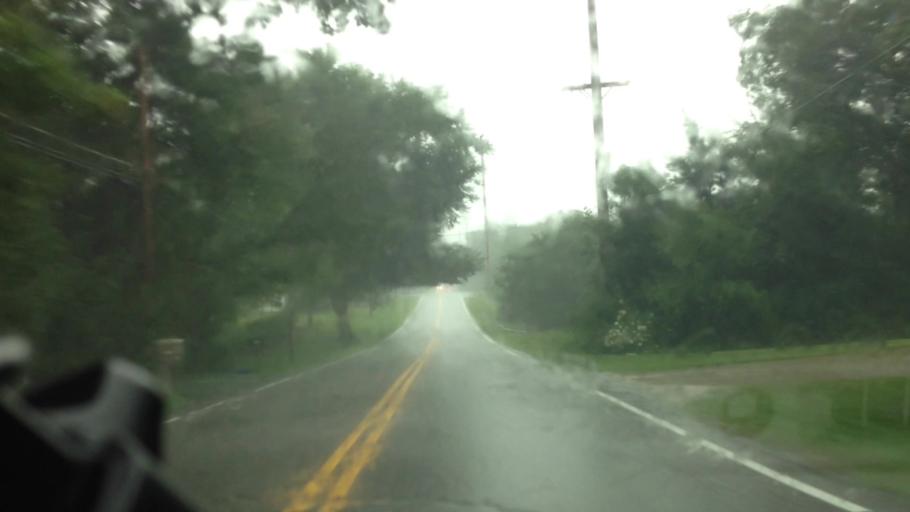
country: US
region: Ohio
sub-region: Stark County
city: Massillon
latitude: 40.8426
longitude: -81.5116
